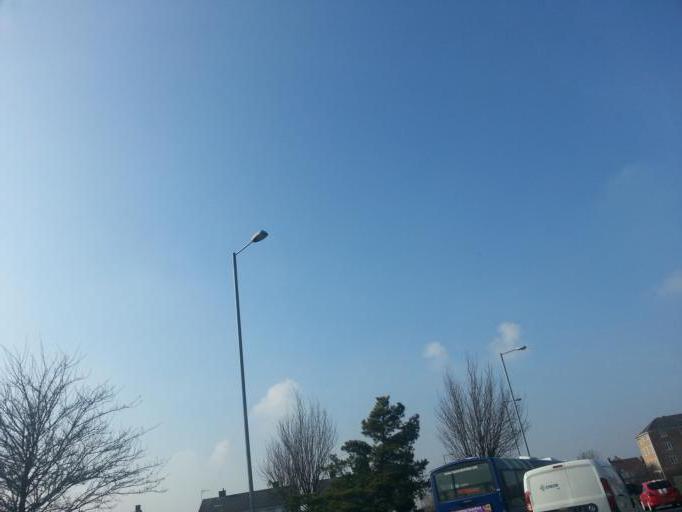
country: GB
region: England
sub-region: Borough of Swindon
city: Swindon
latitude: 51.5673
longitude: -1.7404
